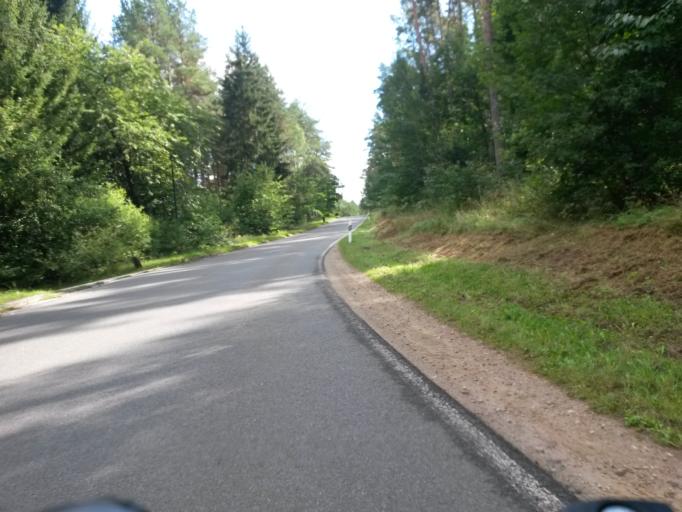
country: DE
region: Brandenburg
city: Templin
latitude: 53.2148
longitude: 13.5208
